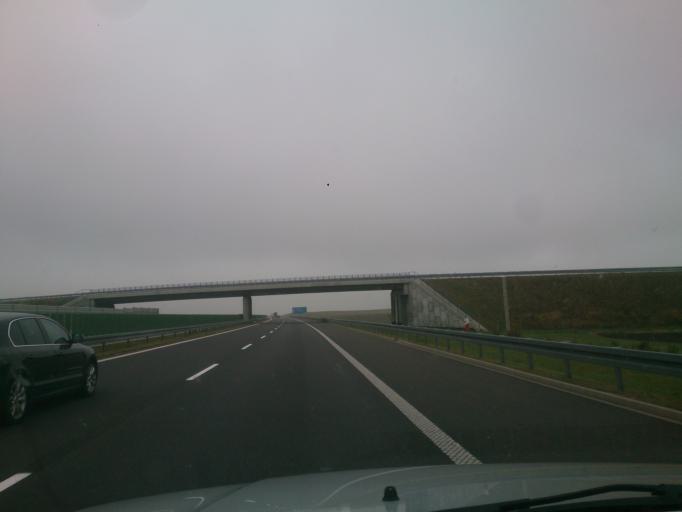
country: PL
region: Pomeranian Voivodeship
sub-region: Powiat starogardzki
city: Smetowo Graniczne
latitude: 53.7151
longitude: 18.6300
